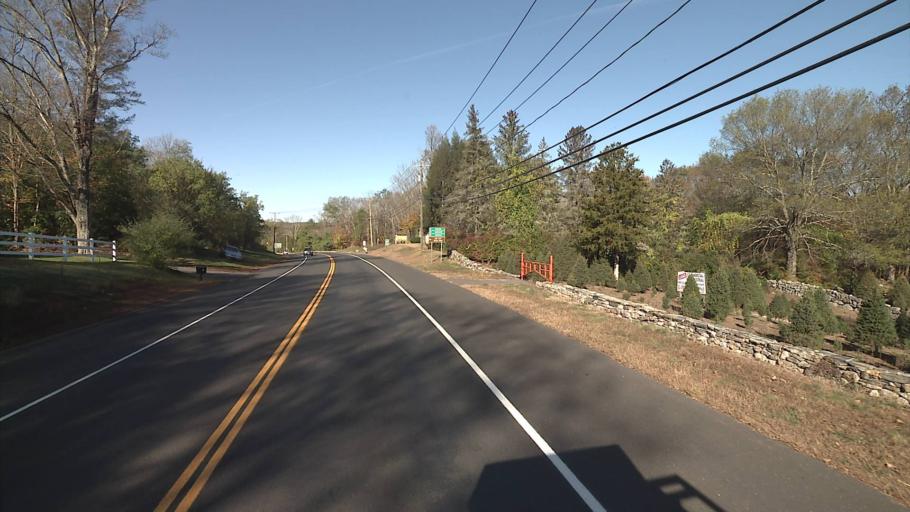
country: US
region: Connecticut
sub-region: Tolland County
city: Coventry Lake
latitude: 41.7381
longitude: -72.3654
